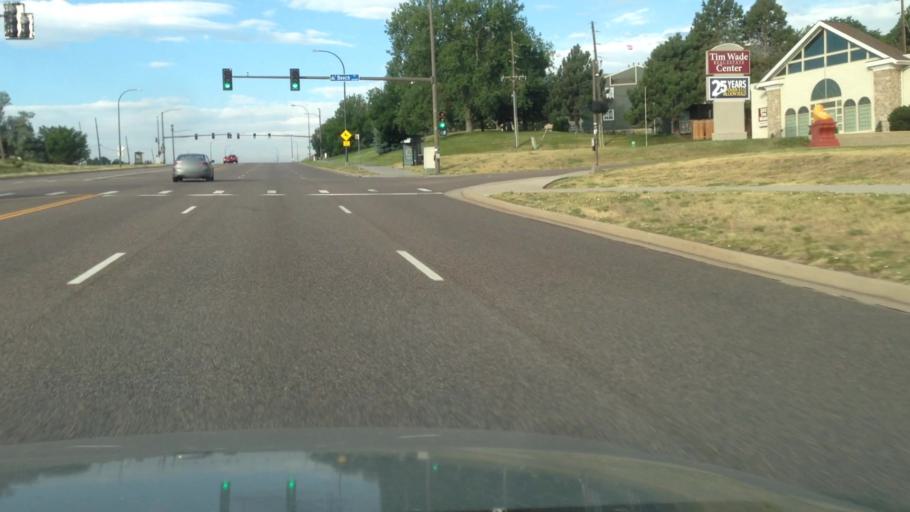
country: US
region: Colorado
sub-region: Jefferson County
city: West Pleasant View
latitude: 39.6951
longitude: -105.1470
